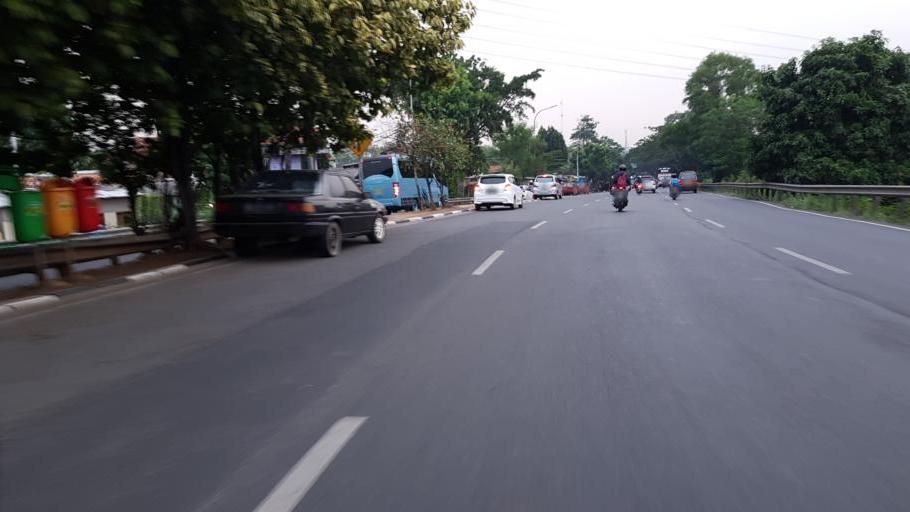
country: ID
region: Jakarta Raya
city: Jakarta
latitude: -6.3080
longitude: 106.8837
